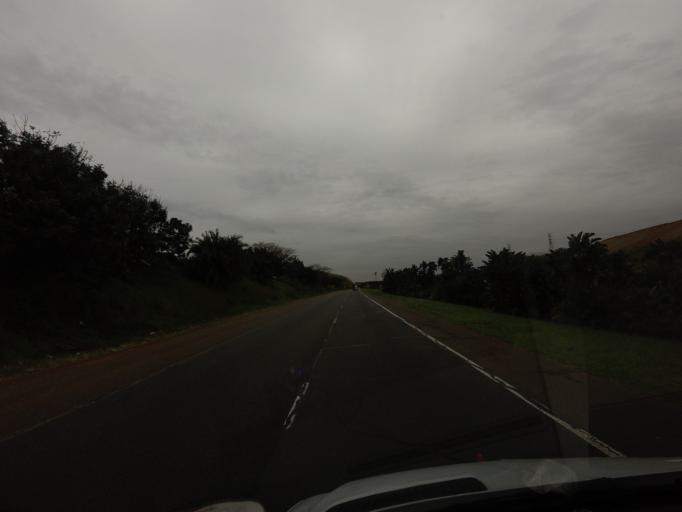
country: ZA
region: KwaZulu-Natal
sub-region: eThekwini Metropolitan Municipality
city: Durban
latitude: -29.7105
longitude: 31.0664
